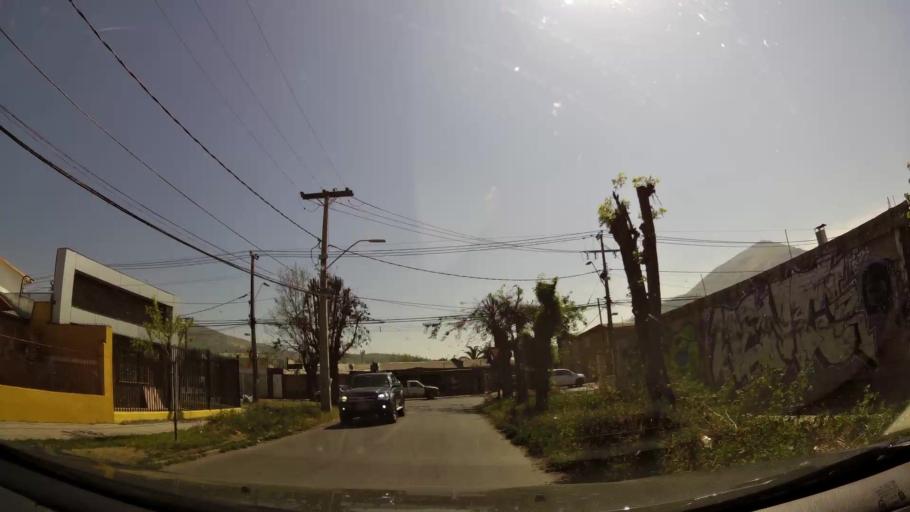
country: CL
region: Santiago Metropolitan
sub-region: Provincia de Santiago
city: Lo Prado
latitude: -33.4047
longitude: -70.7229
